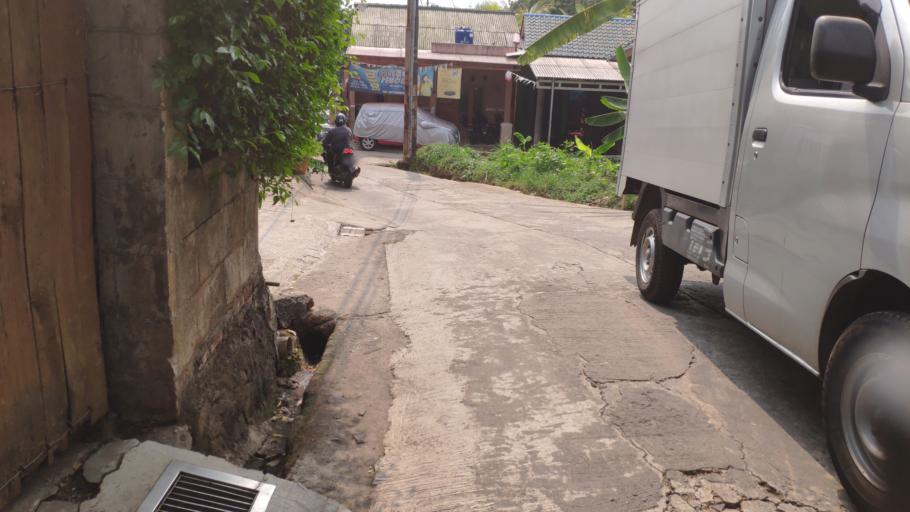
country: ID
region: West Java
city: Depok
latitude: -6.3825
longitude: 106.8014
